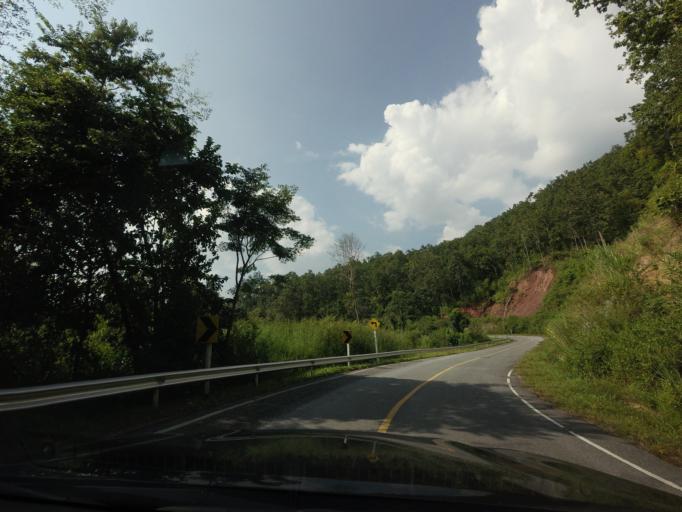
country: TH
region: Uttaradit
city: Ban Khok
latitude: 18.2506
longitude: 100.9966
